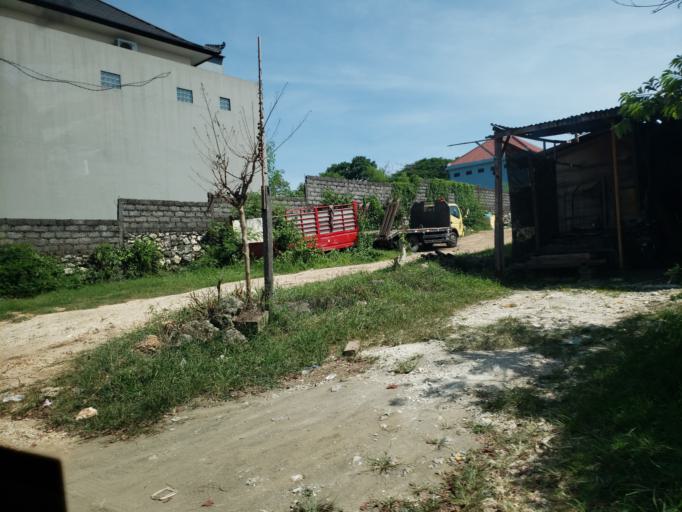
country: ID
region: Bali
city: Kangin
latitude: -8.8307
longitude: 115.1332
